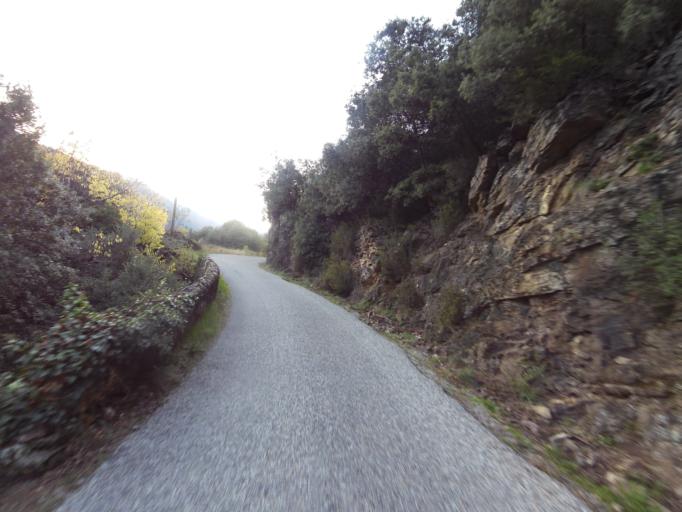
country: FR
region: Rhone-Alpes
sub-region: Departement de l'Ardeche
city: Lablachere
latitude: 44.5268
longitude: 4.1168
